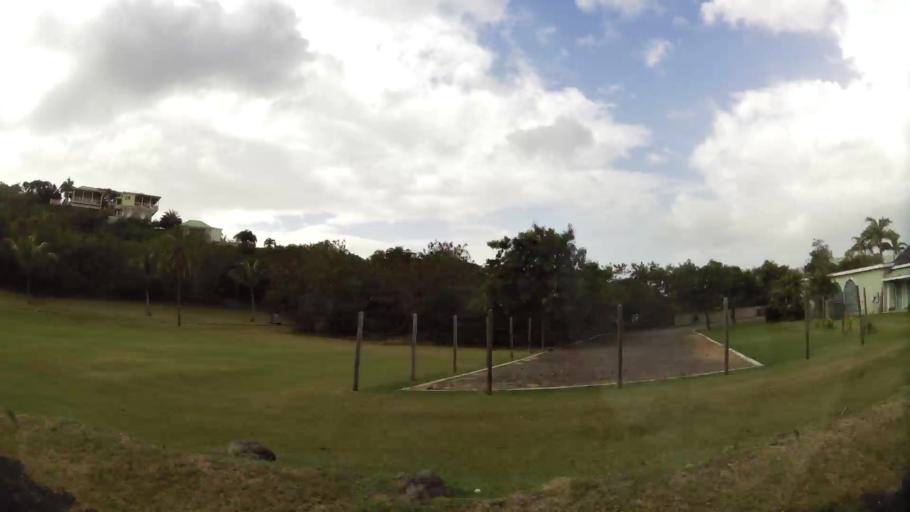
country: KN
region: Saint Thomas Lowland
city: Cotton Ground
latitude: 17.1918
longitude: -62.6166
